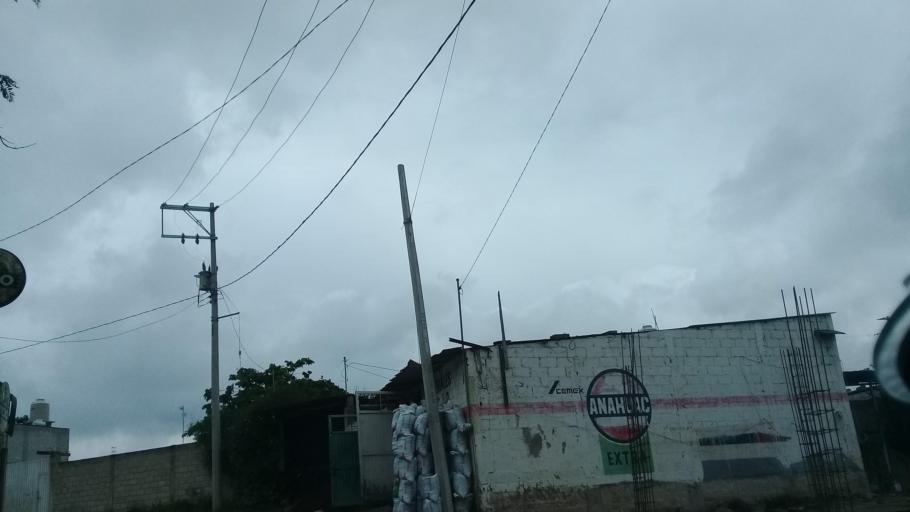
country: MX
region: Veracruz
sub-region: Emiliano Zapata
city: Las Trancas
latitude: 19.4977
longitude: -96.8657
